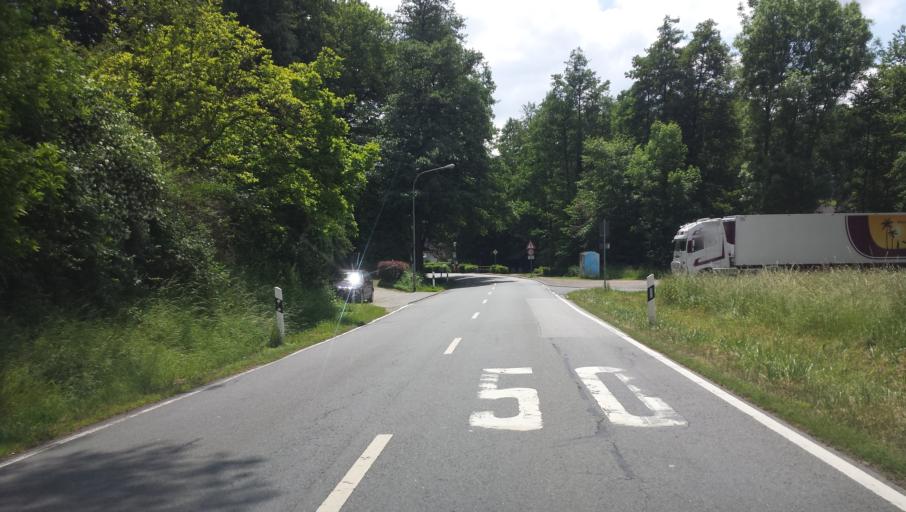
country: DE
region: Hesse
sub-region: Regierungsbezirk Darmstadt
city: Lindenfels
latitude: 49.6772
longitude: 8.7655
